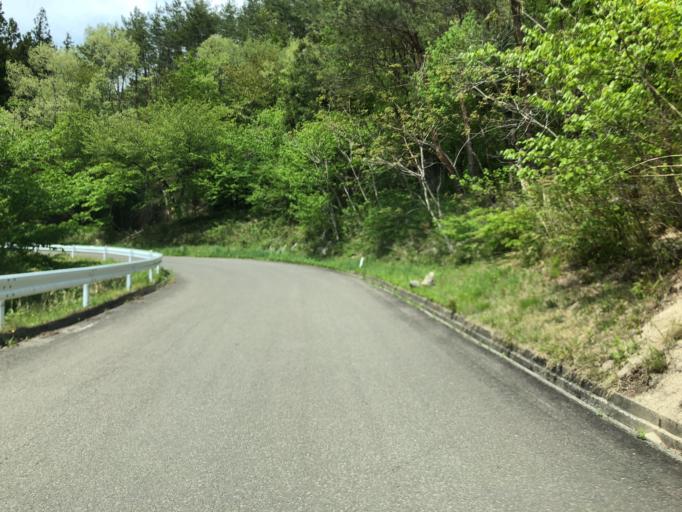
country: JP
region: Fukushima
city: Yanagawamachi-saiwaicho
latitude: 37.7191
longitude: 140.7105
